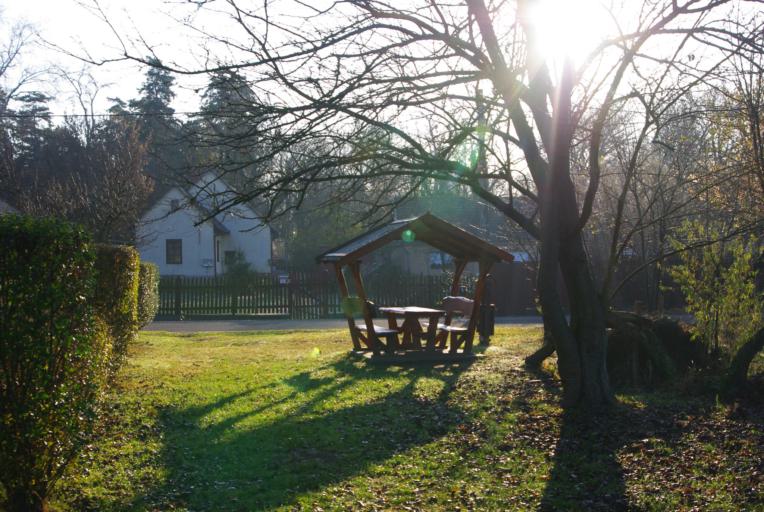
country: HU
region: Pest
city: God
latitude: 47.6859
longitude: 19.1377
